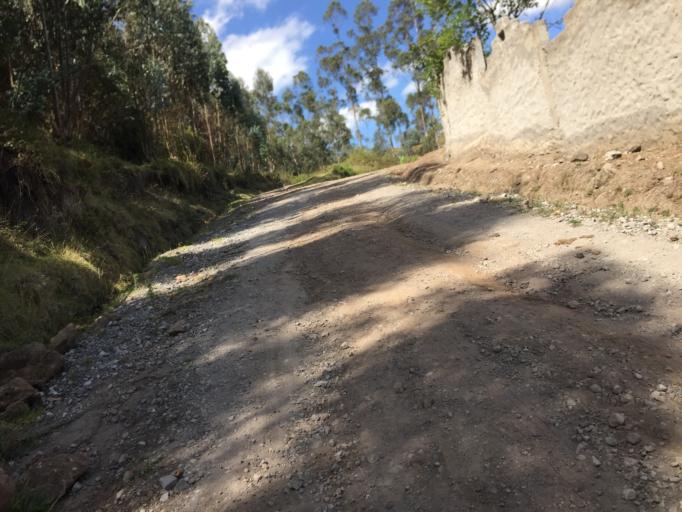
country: EC
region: Imbabura
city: Ibarra
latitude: 0.3085
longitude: -78.1580
